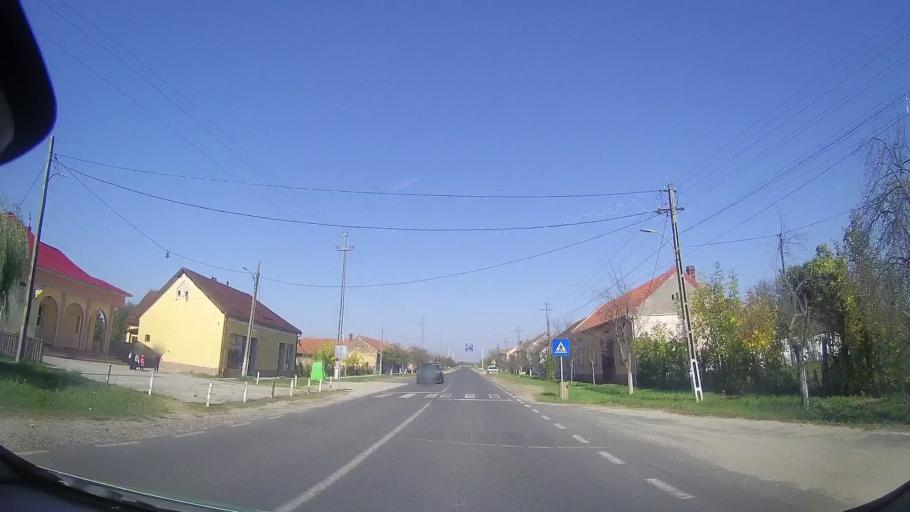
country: RO
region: Timis
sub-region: Comuna Costeiu
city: Costeiu
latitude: 45.7767
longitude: 21.8487
